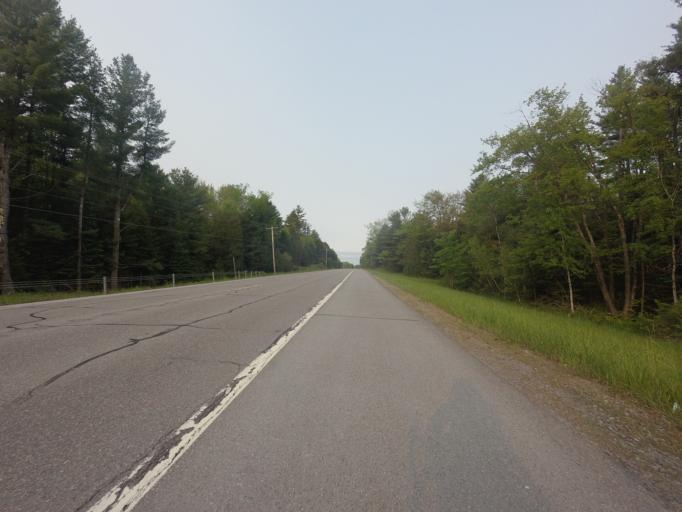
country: US
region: New York
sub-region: Jefferson County
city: Carthage
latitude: 44.0763
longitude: -75.4494
